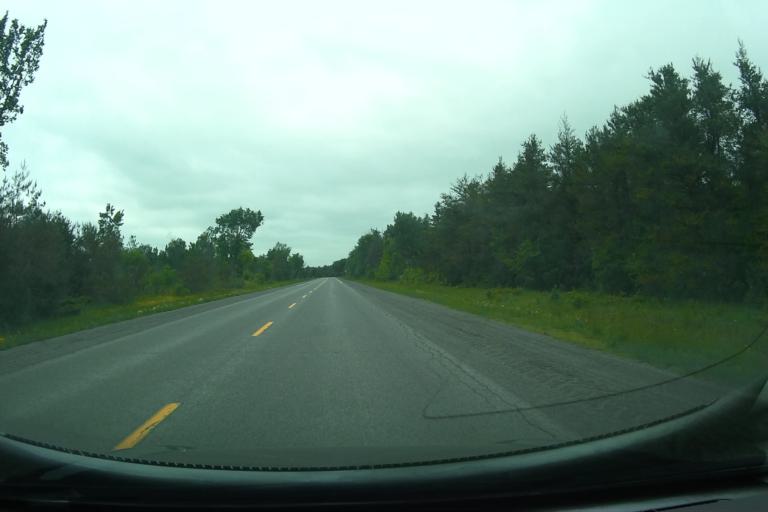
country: CA
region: Ontario
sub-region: Lanark County
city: Smiths Falls
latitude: 45.0144
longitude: -75.8389
